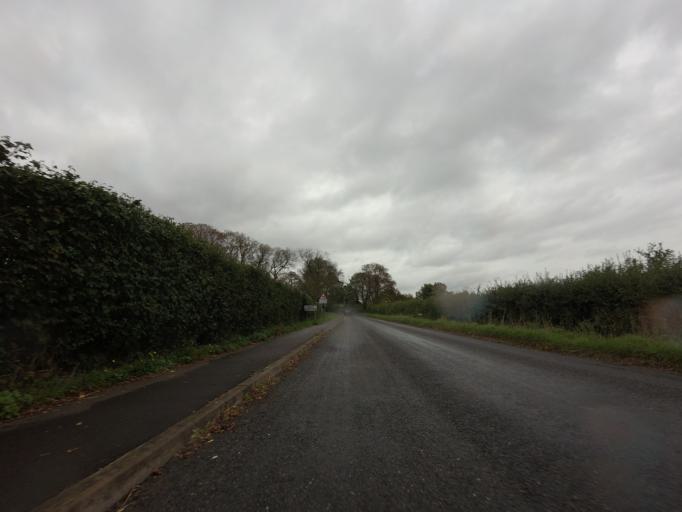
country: GB
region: England
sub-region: Cambridgeshire
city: Comberton
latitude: 52.1610
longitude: -0.0020
